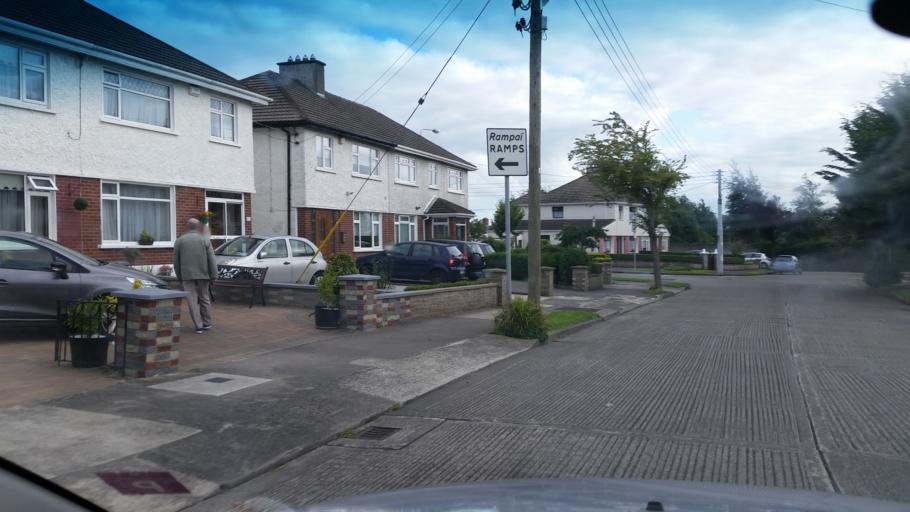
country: IE
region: Leinster
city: Glasnevin
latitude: 53.3868
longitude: -6.2755
